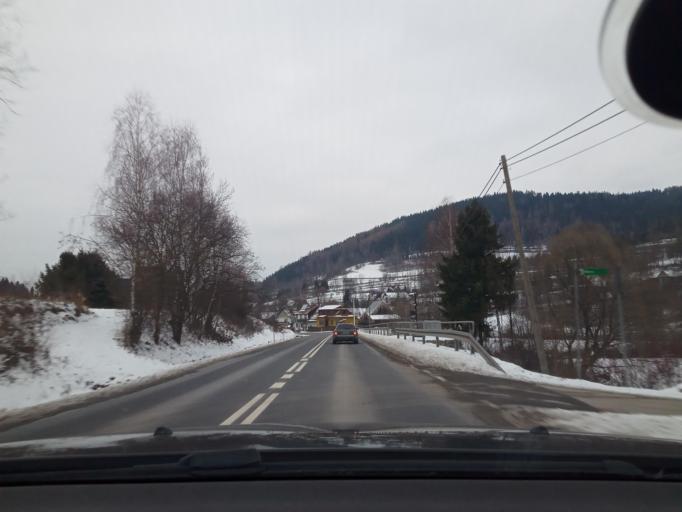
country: PL
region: Lesser Poland Voivodeship
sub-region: Powiat limanowski
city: Lubomierz
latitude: 49.6158
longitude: 20.1841
